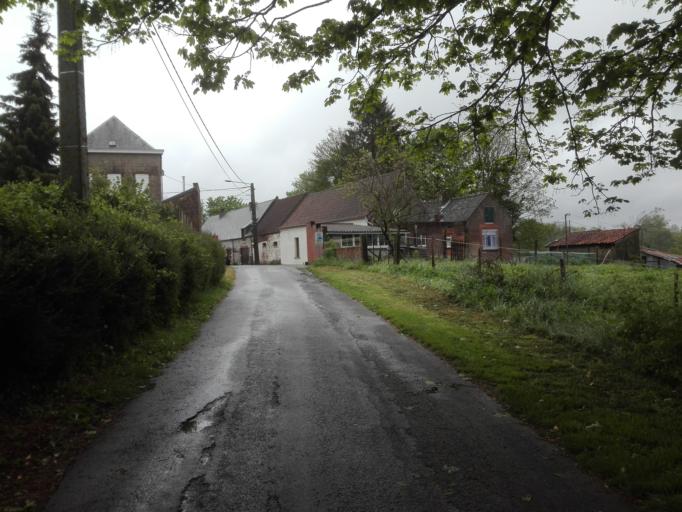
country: BE
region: Wallonia
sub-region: Province du Hainaut
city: Brugelette
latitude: 50.5854
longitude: 3.8795
